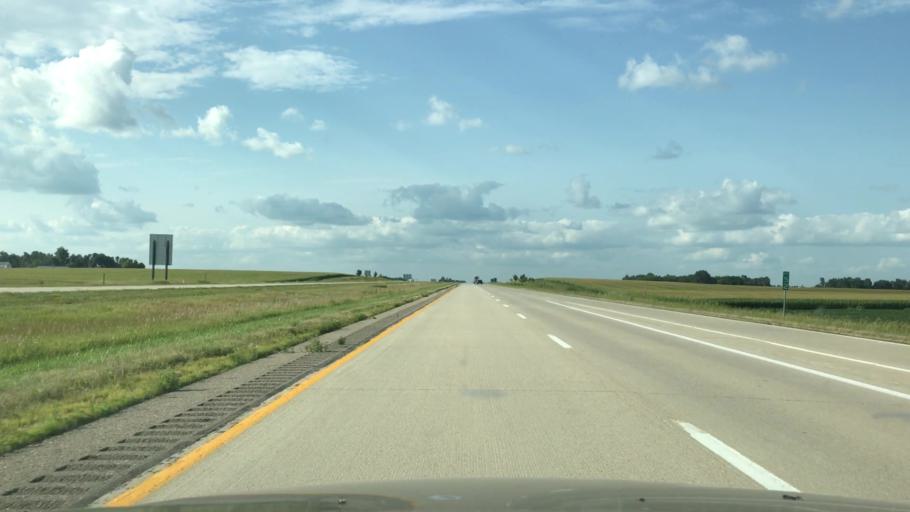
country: US
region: Iowa
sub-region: Osceola County
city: Sibley
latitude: 43.4097
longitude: -95.7170
